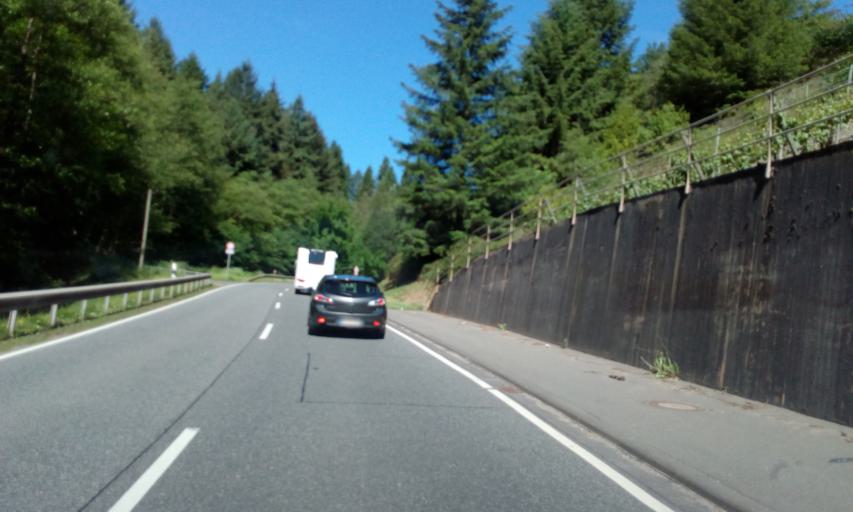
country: DE
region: Rheinland-Pfalz
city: Thornich
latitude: 49.8397
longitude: 6.8296
